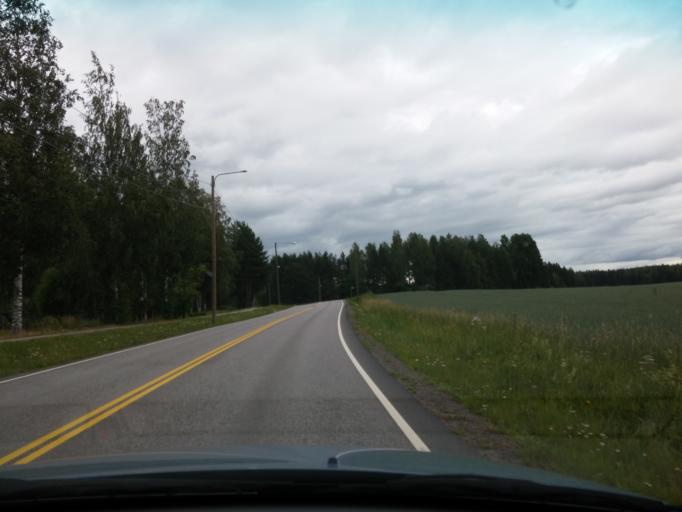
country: FI
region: Uusimaa
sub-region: Porvoo
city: Askola
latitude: 60.4980
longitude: 25.5558
